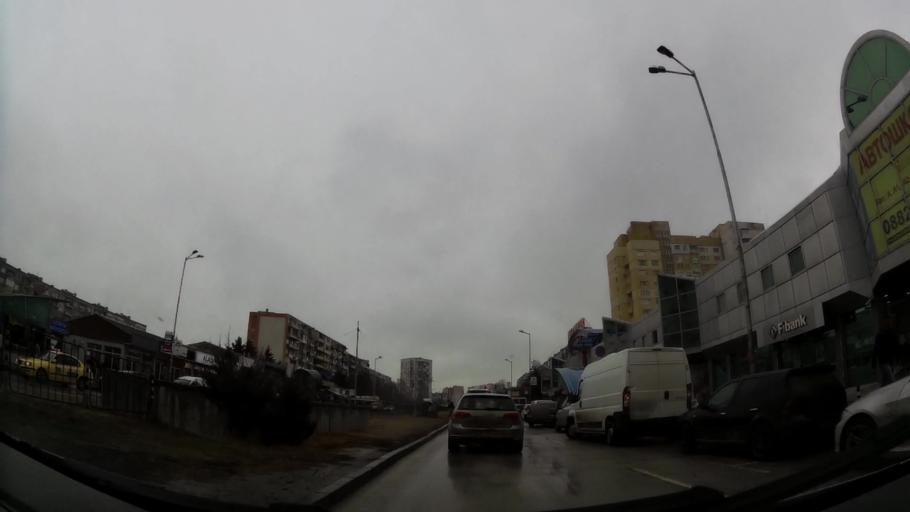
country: BG
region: Sofia-Capital
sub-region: Stolichna Obshtina
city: Sofia
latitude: 42.6529
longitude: 23.3733
